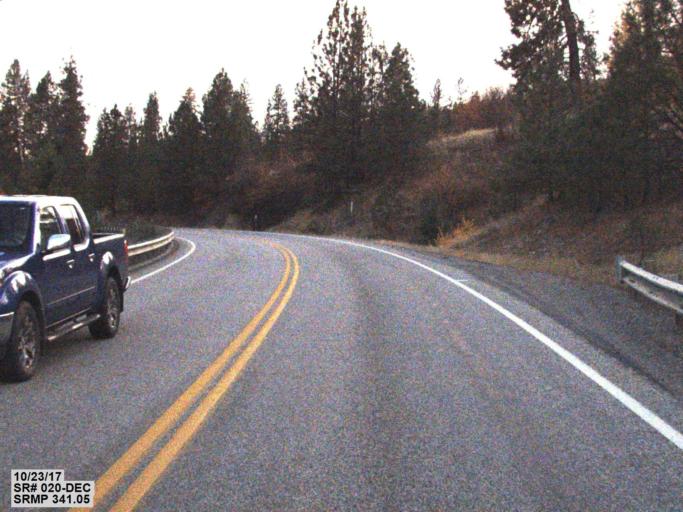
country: US
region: Washington
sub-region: Stevens County
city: Kettle Falls
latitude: 48.6170
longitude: -118.1379
